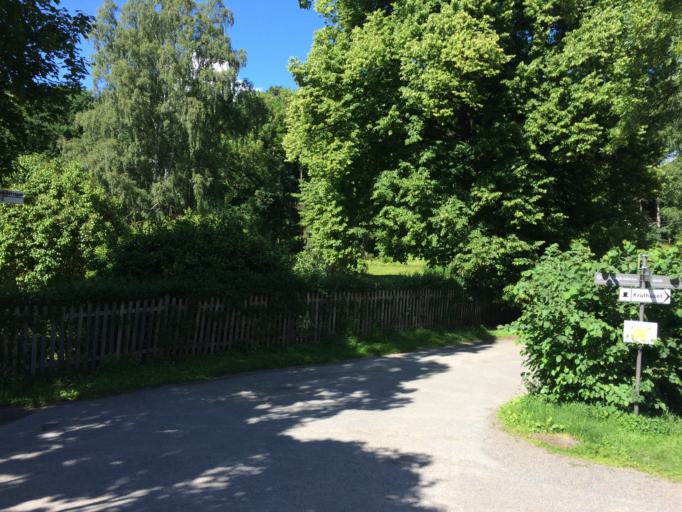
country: SE
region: Stockholm
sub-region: Nacka Kommun
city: Nacka
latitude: 59.3267
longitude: 18.1471
